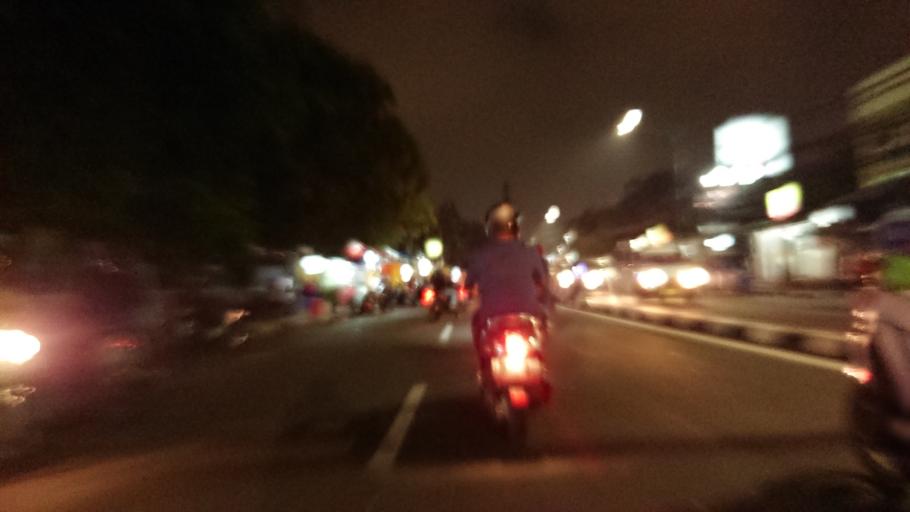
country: ID
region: Jakarta Raya
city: Jakarta
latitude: -6.1888
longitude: 106.8079
